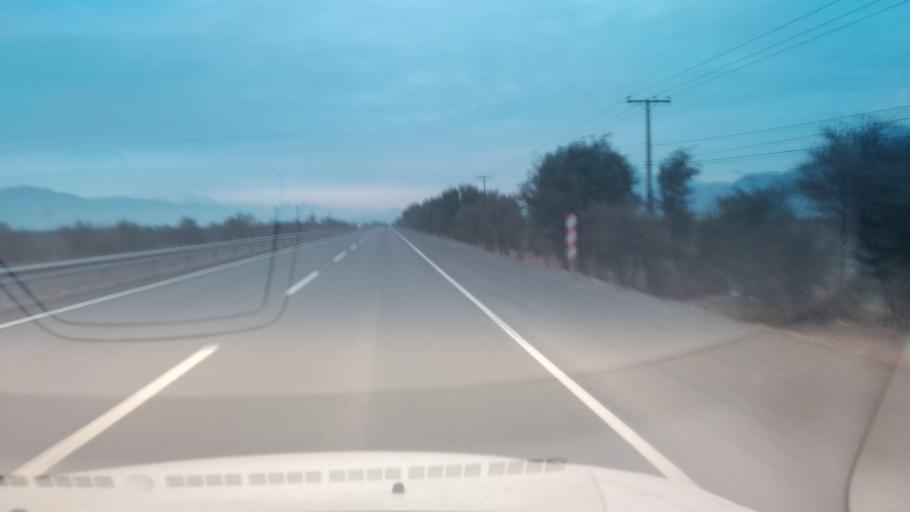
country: CL
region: Santiago Metropolitan
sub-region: Provincia de Chacabuco
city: Chicureo Abajo
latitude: -33.1022
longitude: -70.6910
